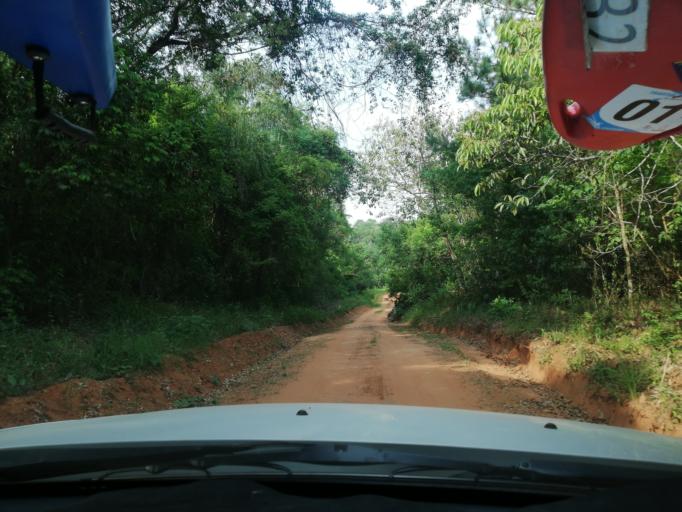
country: AR
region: Misiones
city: Santa Ana
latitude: -27.3058
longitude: -55.5815
